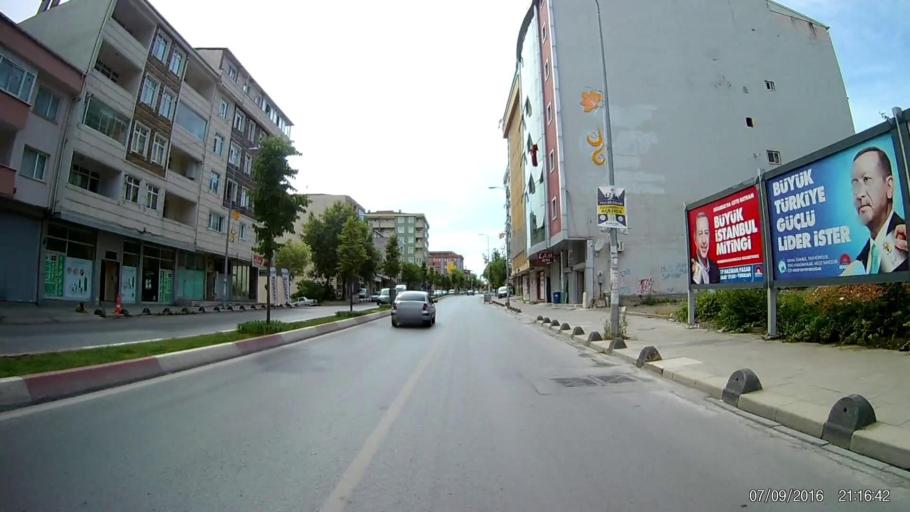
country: TR
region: Istanbul
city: Sultanbeyli
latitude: 40.9625
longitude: 29.2884
